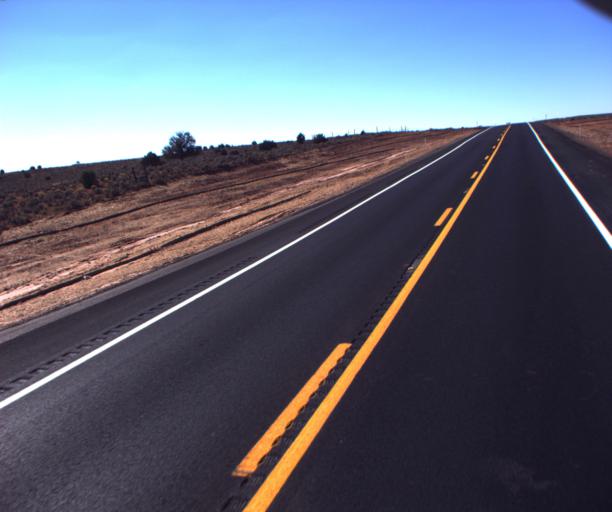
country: US
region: Arizona
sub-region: Apache County
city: Ganado
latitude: 35.7183
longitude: -109.4656
